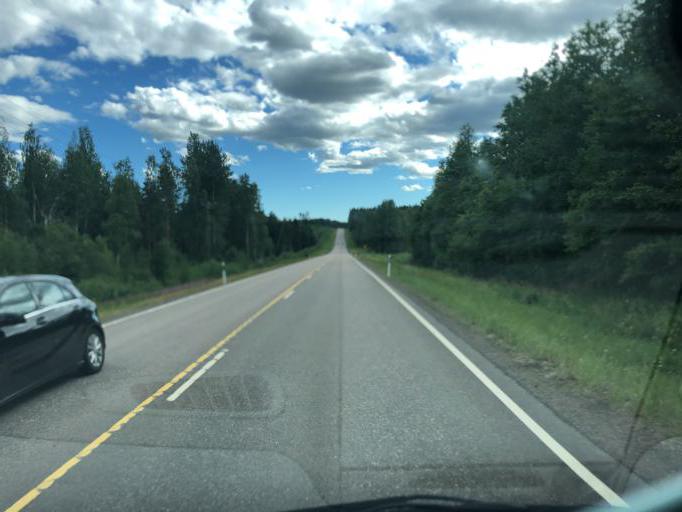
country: FI
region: Southern Savonia
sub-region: Mikkeli
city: Maentyharju
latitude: 61.0818
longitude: 27.0630
